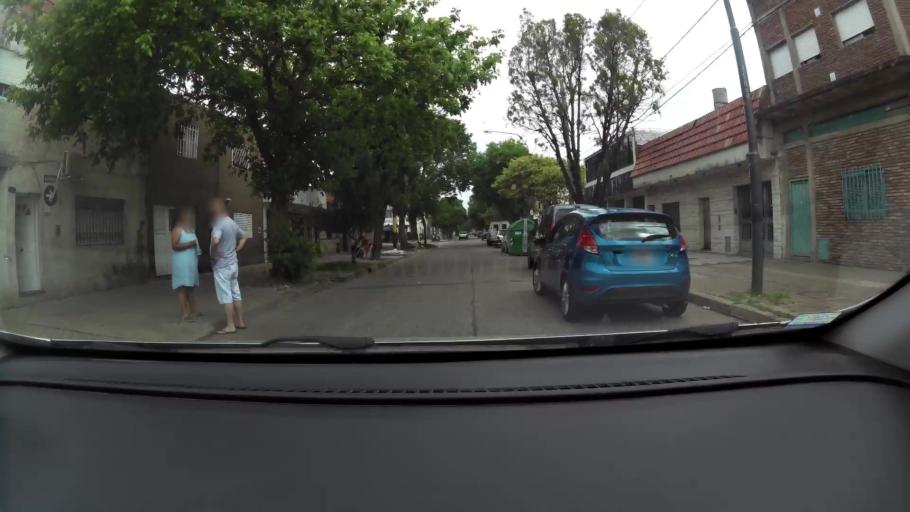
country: AR
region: Santa Fe
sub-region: Departamento de Rosario
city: Rosario
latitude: -32.9732
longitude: -60.6536
